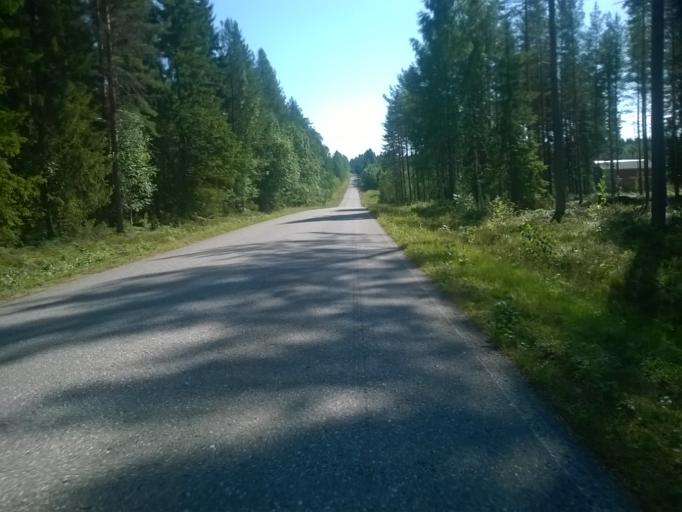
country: FI
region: Kainuu
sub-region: Kehys-Kainuu
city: Kuhmo
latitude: 64.1331
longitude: 29.4378
